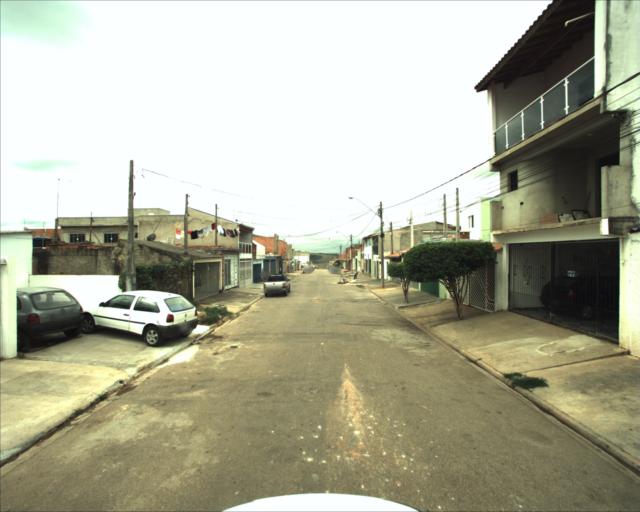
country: BR
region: Sao Paulo
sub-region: Sorocaba
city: Sorocaba
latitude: -23.4329
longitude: -47.5057
